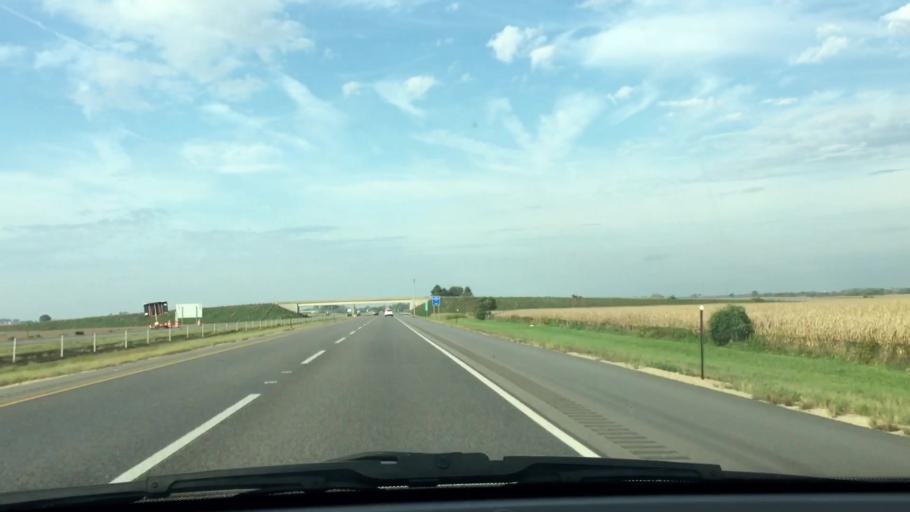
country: US
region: Illinois
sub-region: Ogle County
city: Rochelle
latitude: 41.8829
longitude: -89.1271
